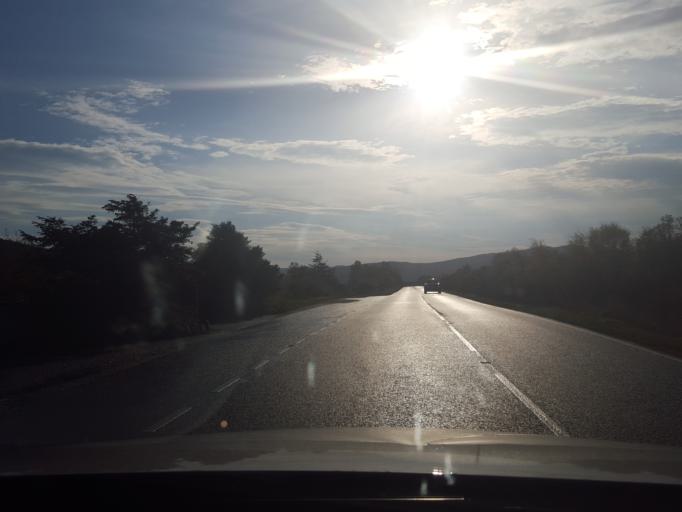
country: GB
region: Scotland
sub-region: Highland
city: Portree
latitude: 57.2570
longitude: -5.9404
